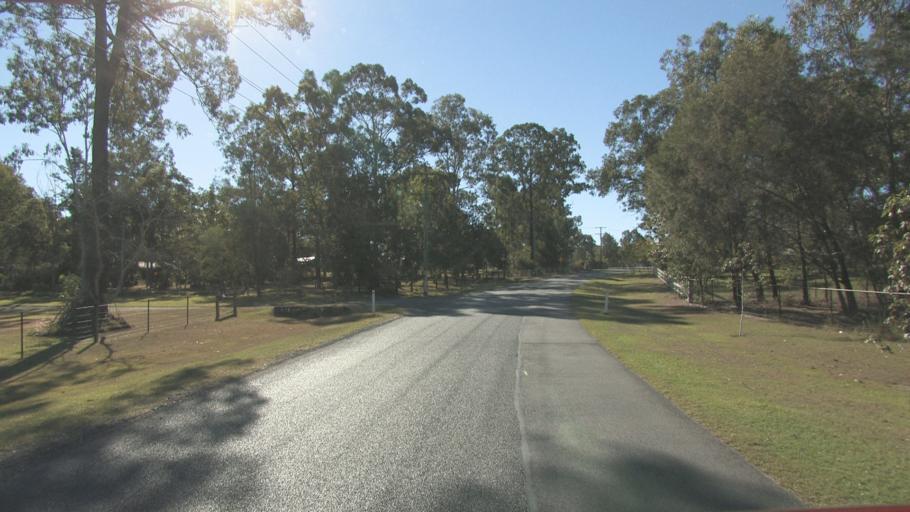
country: AU
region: Queensland
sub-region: Logan
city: Park Ridge South
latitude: -27.7290
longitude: 153.0202
